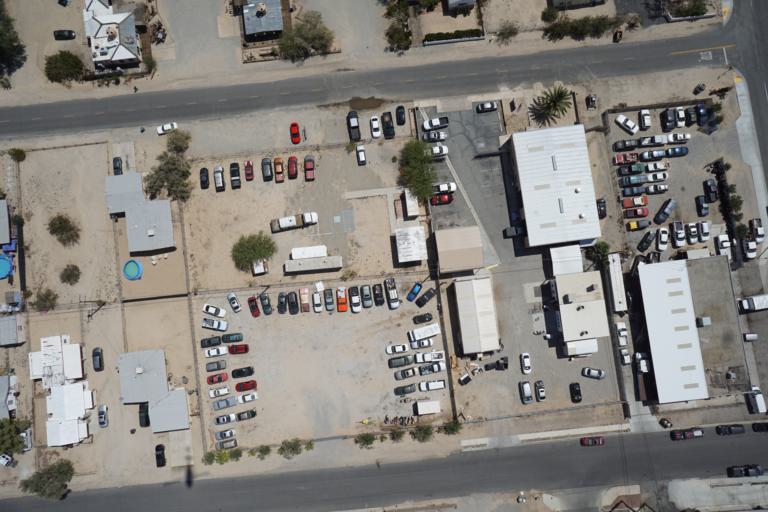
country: US
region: California
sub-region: San Bernardino County
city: Twentynine Palms
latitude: 34.1365
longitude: -116.0520
